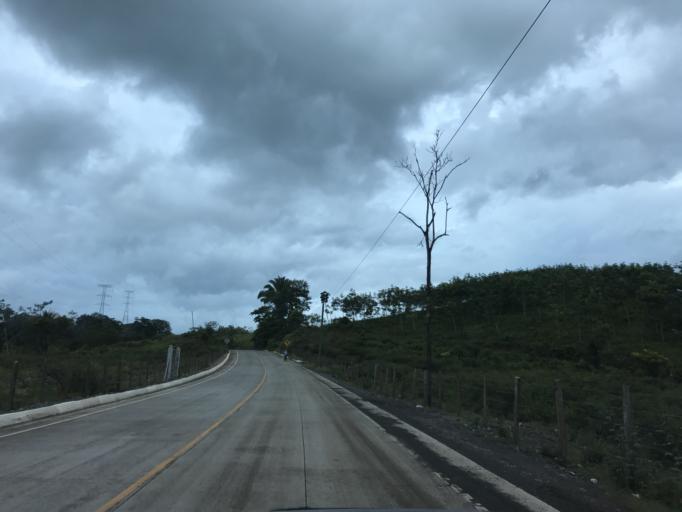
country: GT
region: Izabal
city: Morales
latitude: 15.6365
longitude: -89.0431
